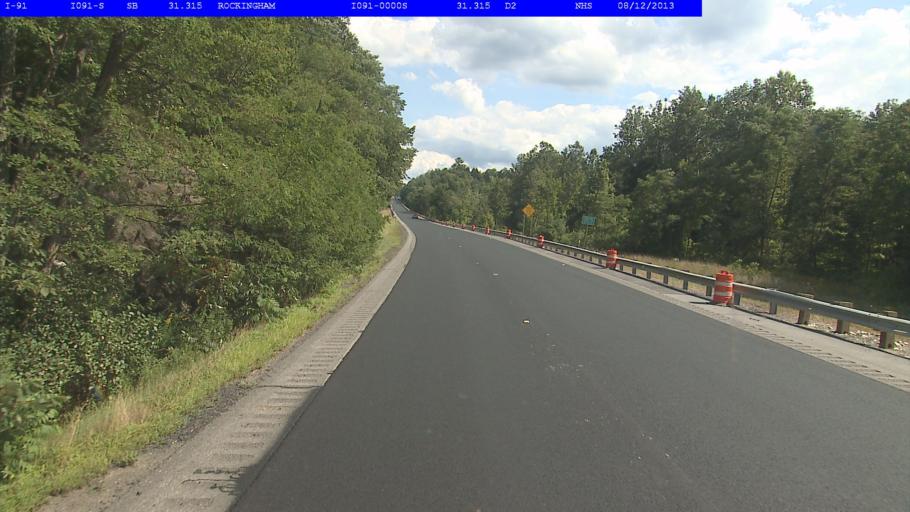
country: US
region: Vermont
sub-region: Windham County
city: Bellows Falls
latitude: 43.1261
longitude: -72.4720
